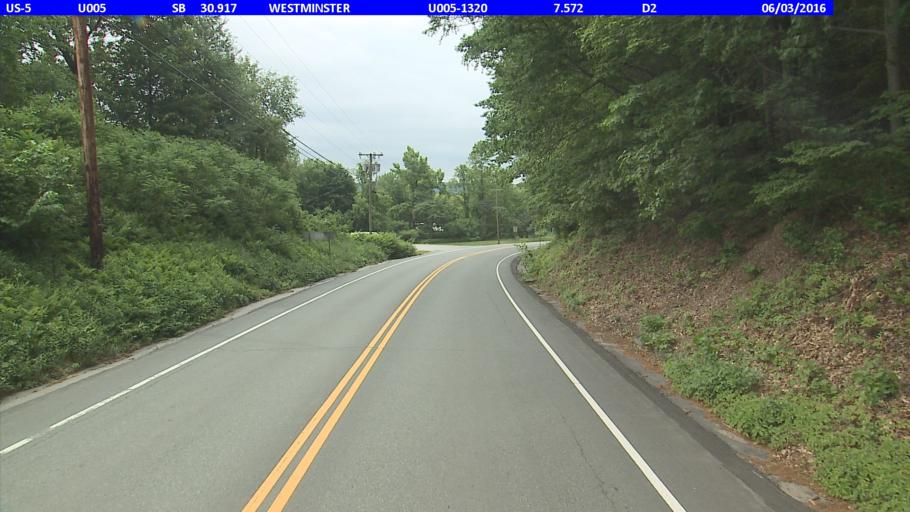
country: US
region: Vermont
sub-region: Windham County
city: Bellows Falls
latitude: 43.1173
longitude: -72.4371
